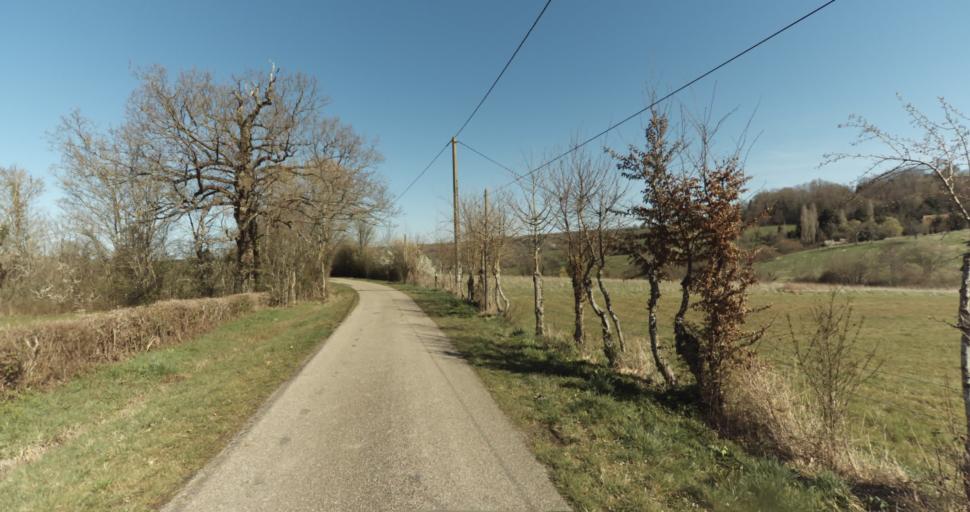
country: FR
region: Lower Normandy
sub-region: Departement du Calvados
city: Livarot
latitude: 48.9426
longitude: 0.0722
